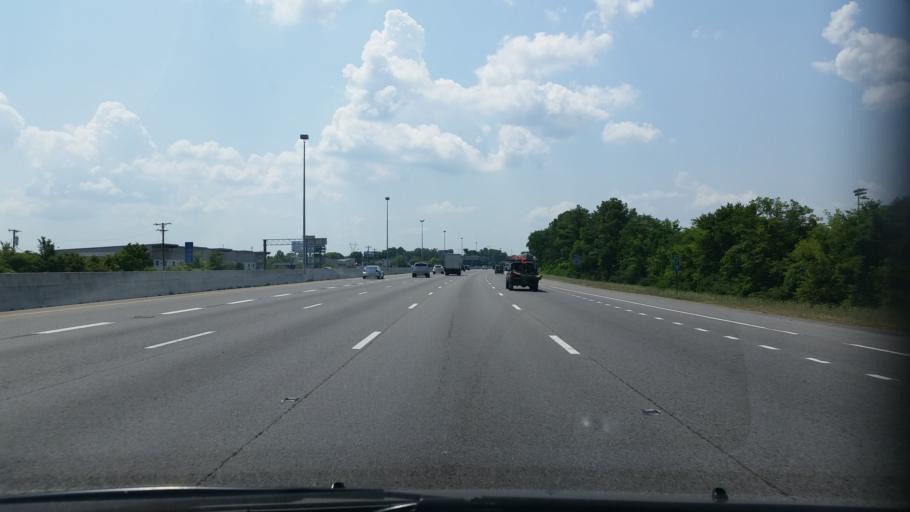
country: US
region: Tennessee
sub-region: Davidson County
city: Oak Hill
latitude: 36.0995
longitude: -86.7642
